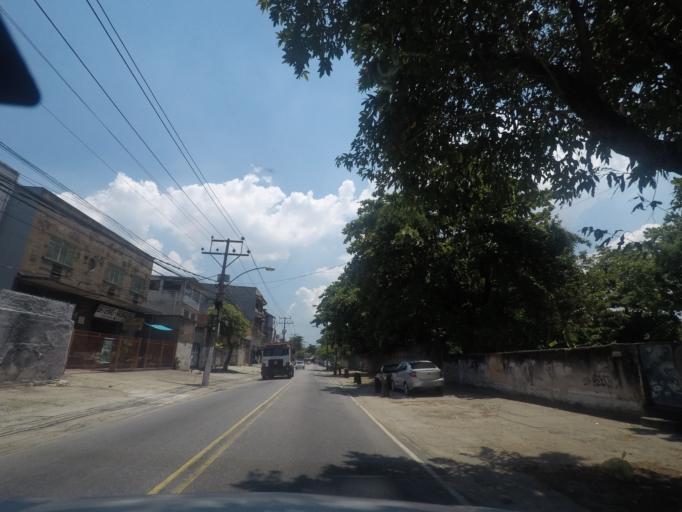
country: BR
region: Rio de Janeiro
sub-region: Duque De Caxias
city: Duque de Caxias
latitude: -22.8197
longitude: -43.3053
